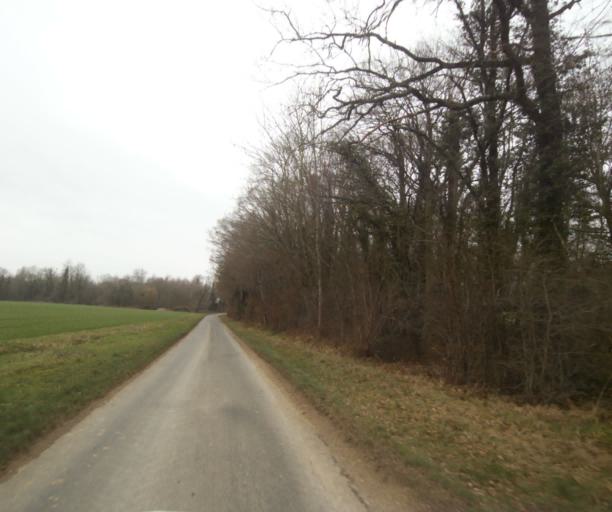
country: FR
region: Champagne-Ardenne
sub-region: Departement de la Haute-Marne
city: Villiers-en-Lieu
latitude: 48.6342
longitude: 4.8128
